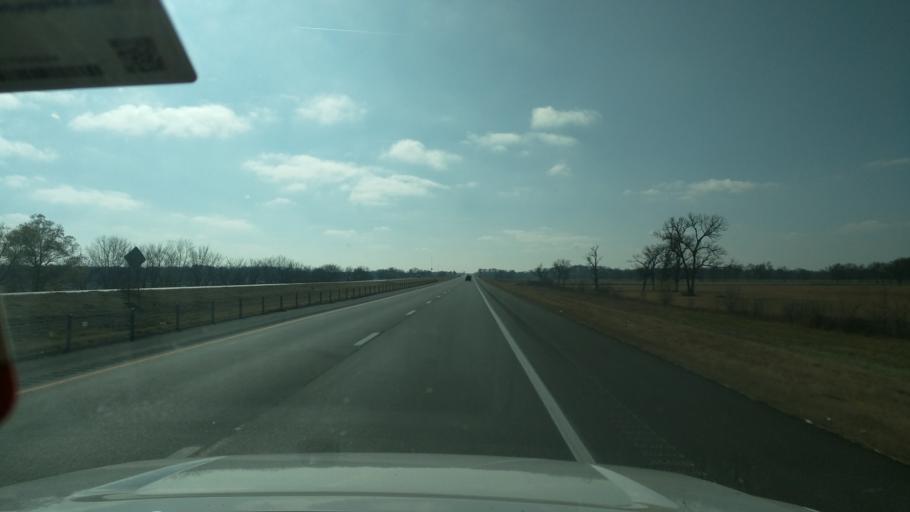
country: US
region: Oklahoma
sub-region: Washington County
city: Bartlesville
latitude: 36.6610
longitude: -95.9356
